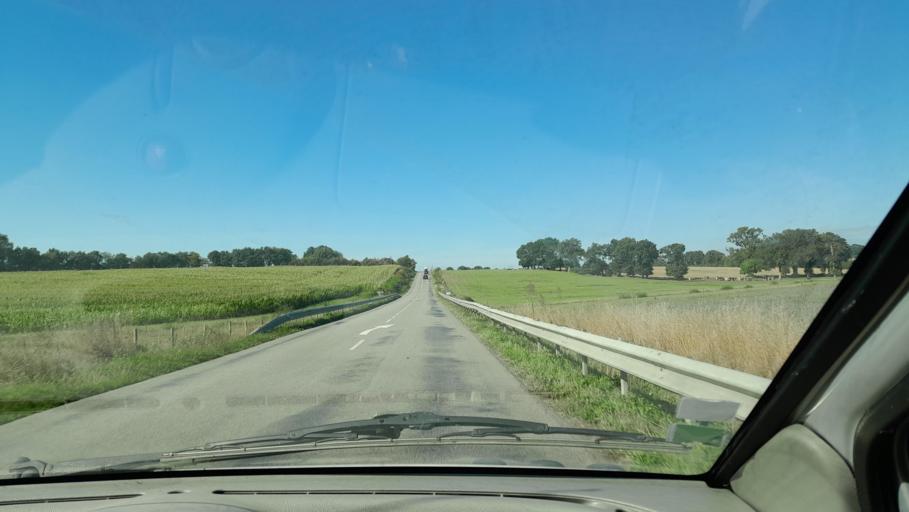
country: FR
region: Pays de la Loire
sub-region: Departement de la Mayenne
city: Ballots
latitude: 47.9568
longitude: -1.0581
